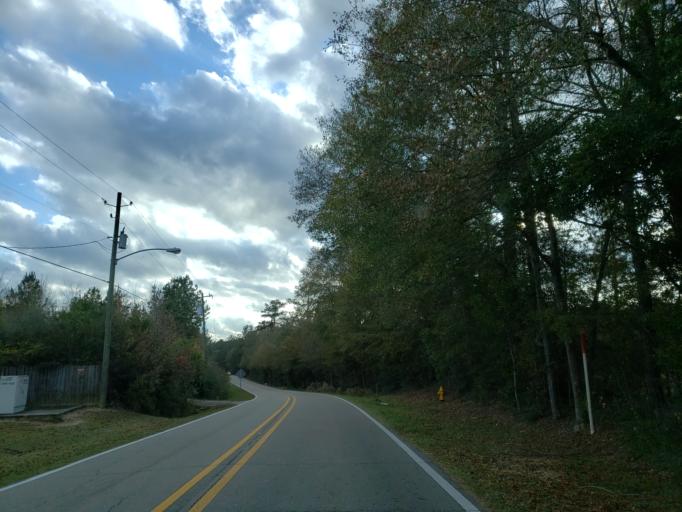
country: US
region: Mississippi
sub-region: Forrest County
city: Hattiesburg
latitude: 31.2766
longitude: -89.2906
